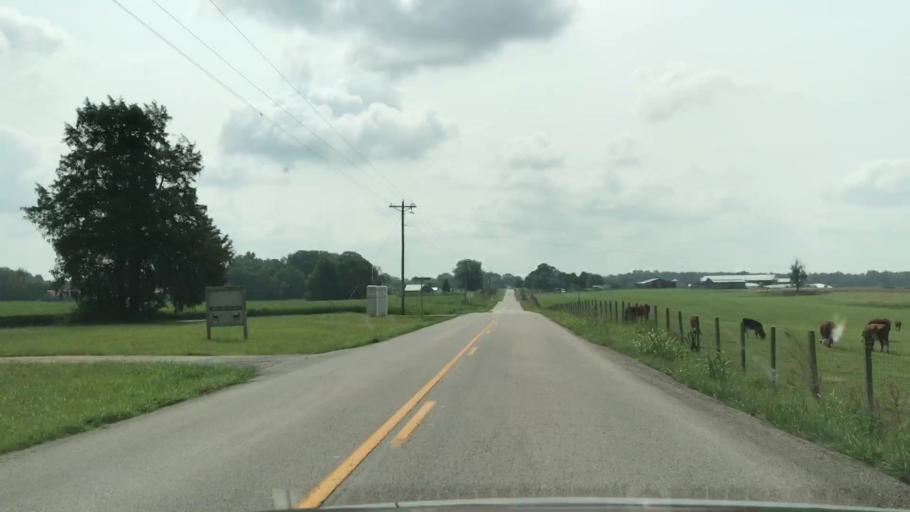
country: US
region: Kentucky
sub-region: Edmonson County
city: Brownsville
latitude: 37.1395
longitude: -86.1801
